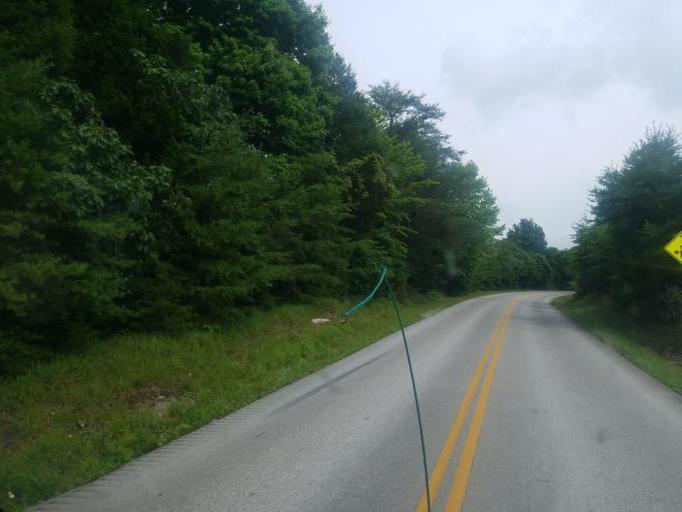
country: US
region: Kentucky
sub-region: Hart County
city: Munfordville
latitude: 37.2970
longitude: -86.0612
